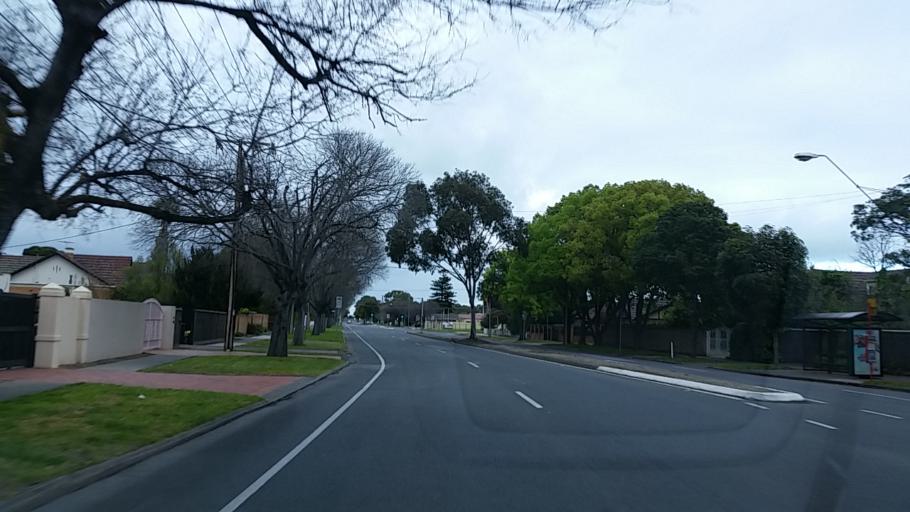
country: AU
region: South Australia
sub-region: Charles Sturt
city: Findon
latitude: -34.9261
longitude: 138.5292
